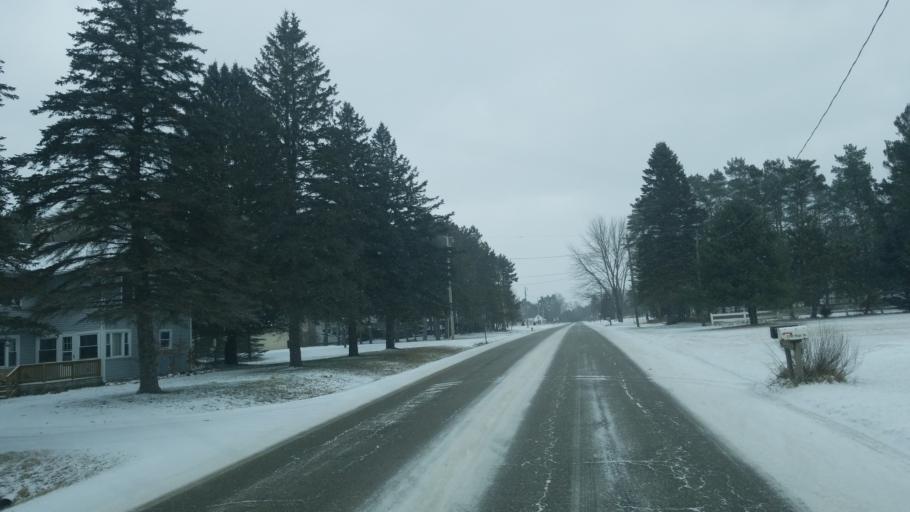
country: US
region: Michigan
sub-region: Osceola County
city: Evart
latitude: 43.9125
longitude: -85.2559
